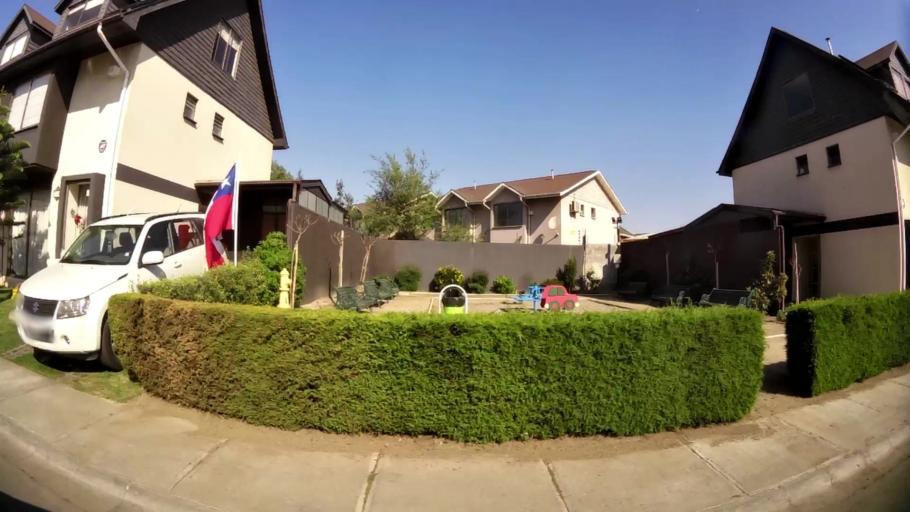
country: CL
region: Santiago Metropolitan
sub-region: Provincia de Santiago
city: Lo Prado
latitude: -33.4829
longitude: -70.7675
